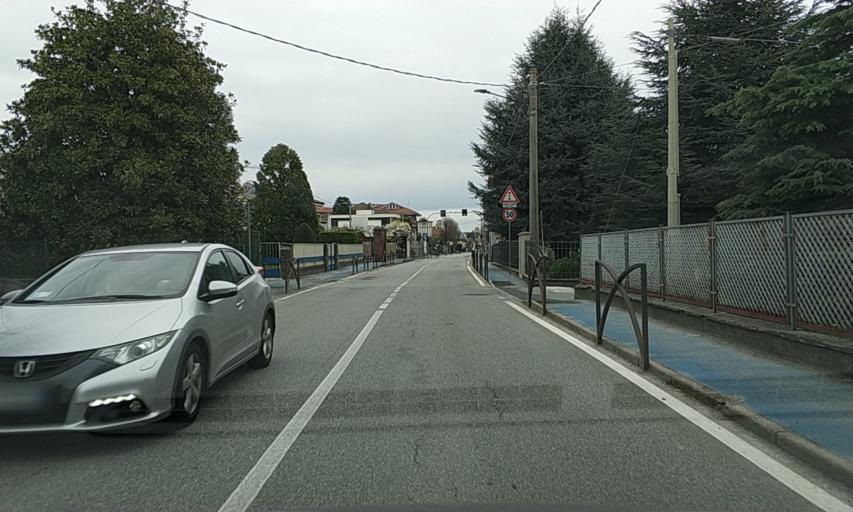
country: IT
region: Piedmont
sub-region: Provincia di Torino
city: Rivarolo Canavese
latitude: 45.3314
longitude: 7.7133
